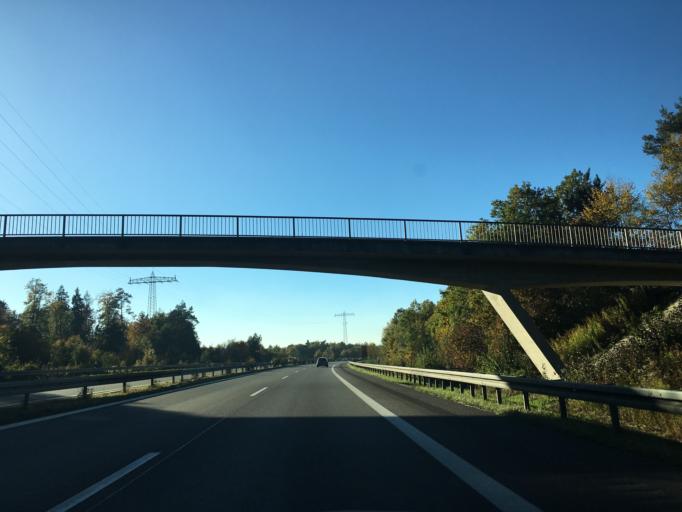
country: DE
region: Baden-Wuerttemberg
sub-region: Freiburg Region
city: Steisslingen
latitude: 47.7694
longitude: 8.9206
